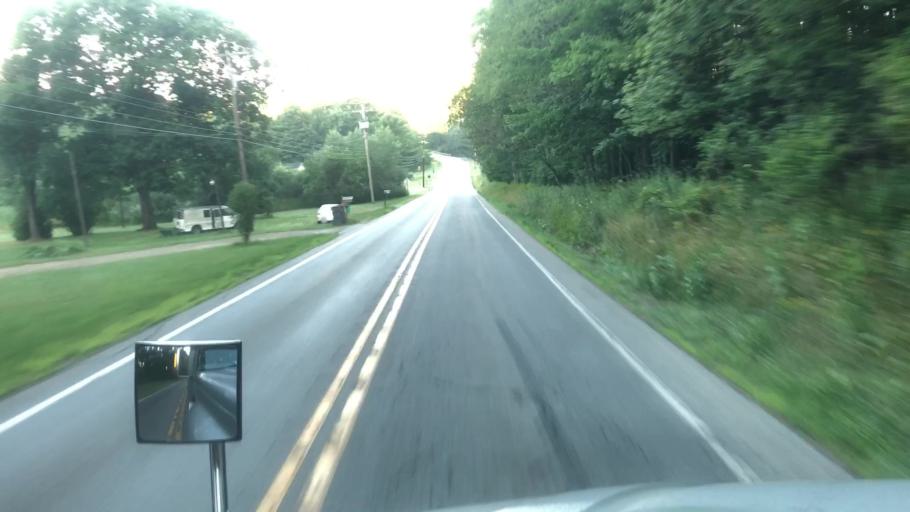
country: US
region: Pennsylvania
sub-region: Venango County
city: Hasson Heights
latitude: 41.5060
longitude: -79.6293
